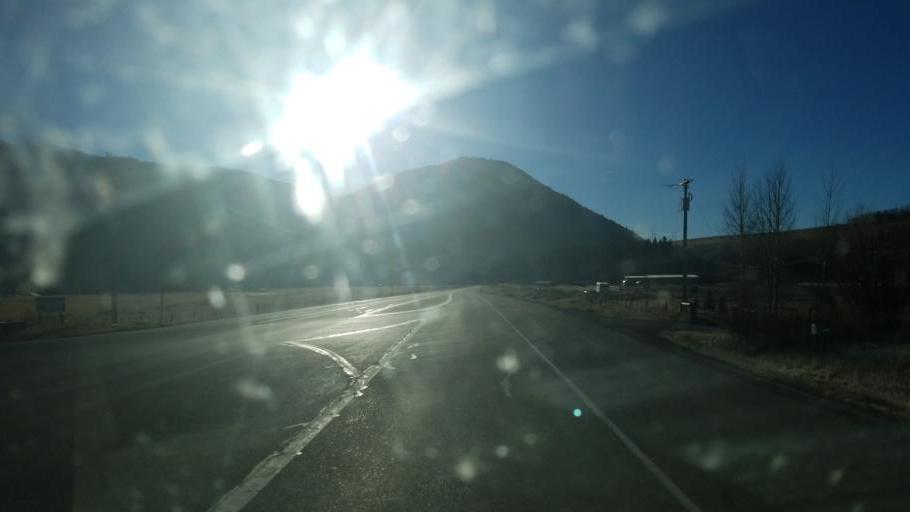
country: US
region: Colorado
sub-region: Gunnison County
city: Crested Butte
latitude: 38.8045
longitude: -106.8908
